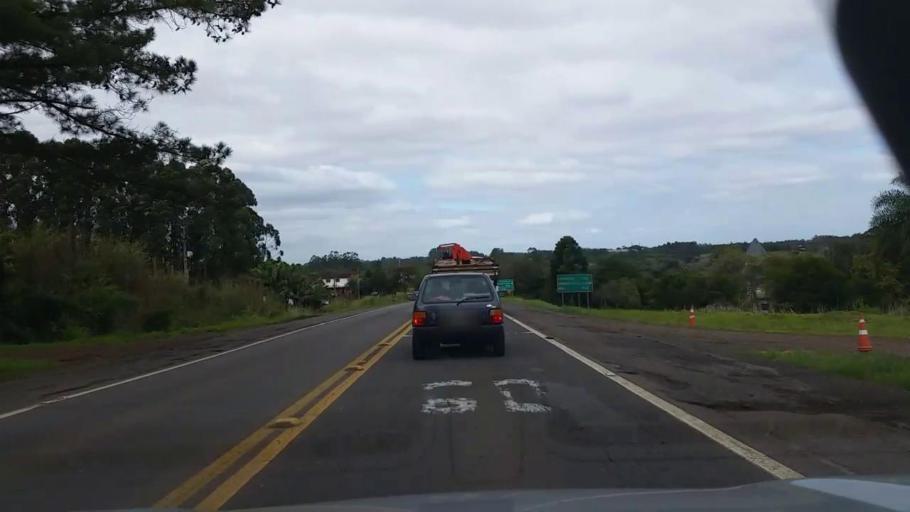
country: BR
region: Rio Grande do Sul
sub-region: Arroio Do Meio
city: Arroio do Meio
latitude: -29.4031
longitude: -52.0379
